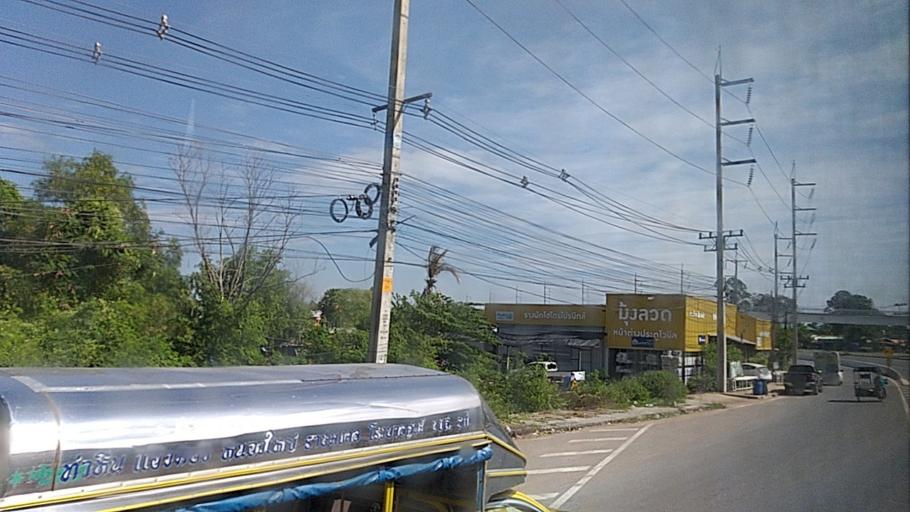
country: TH
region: Khon Kaen
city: Khon Kaen
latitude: 16.4379
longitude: 102.9419
